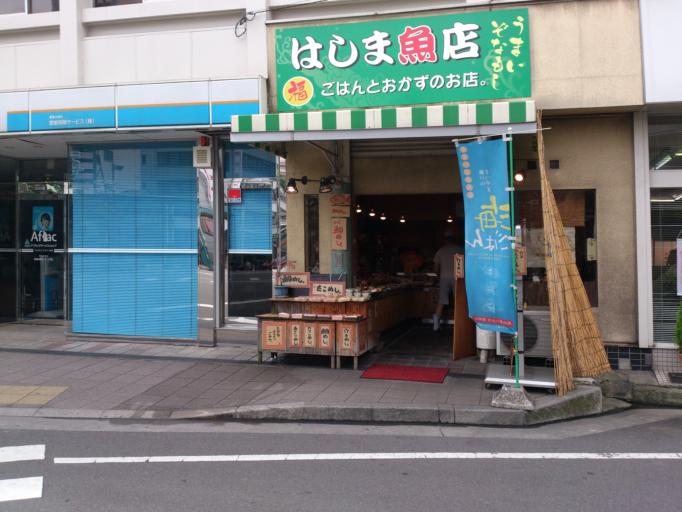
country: JP
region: Ehime
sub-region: Shikoku-chuo Shi
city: Matsuyama
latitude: 33.8363
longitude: 132.7618
